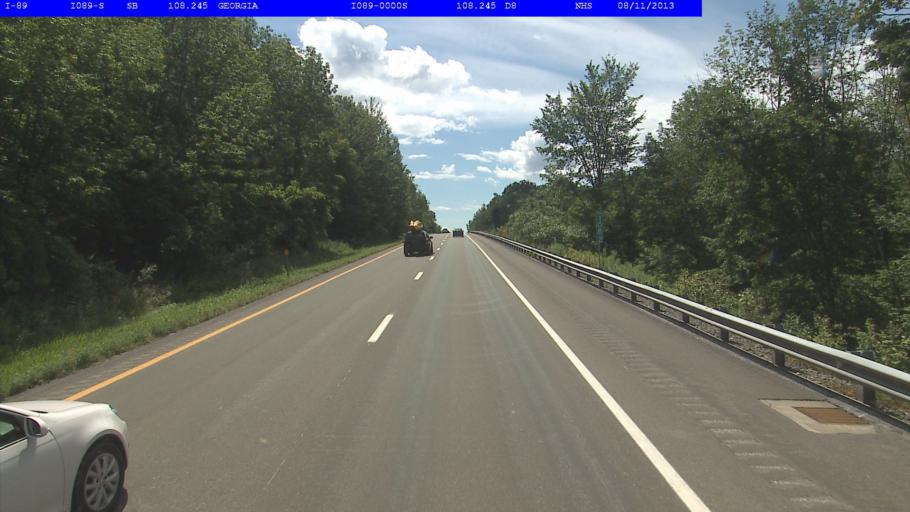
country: US
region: Vermont
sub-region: Chittenden County
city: Milton
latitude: 44.7165
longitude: -73.0856
